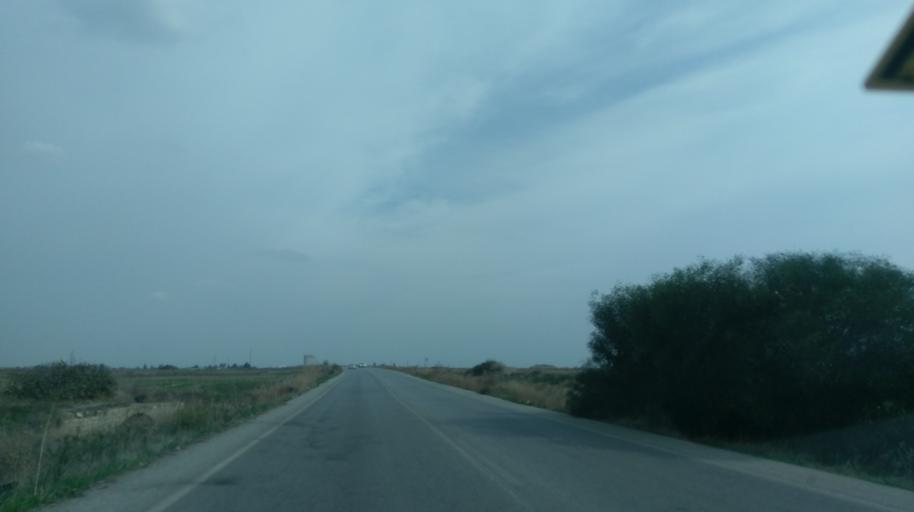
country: CY
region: Ammochostos
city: Lefkonoiko
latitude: 35.2565
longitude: 33.7038
